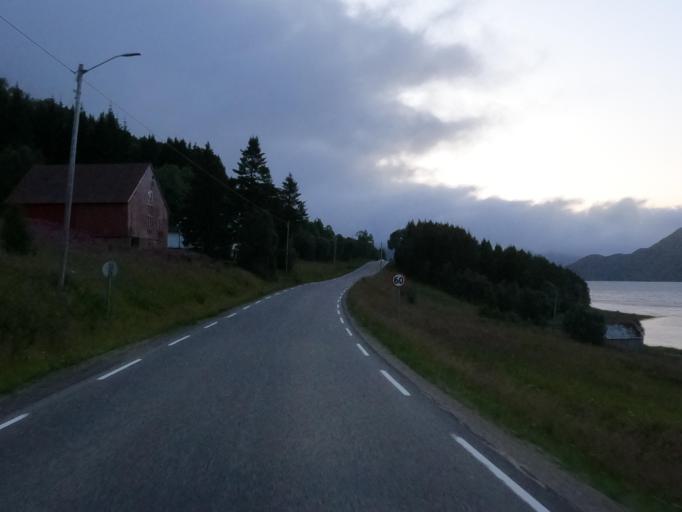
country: NO
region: Nordland
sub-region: Lodingen
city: Lodingen
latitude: 68.5858
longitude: 15.7912
